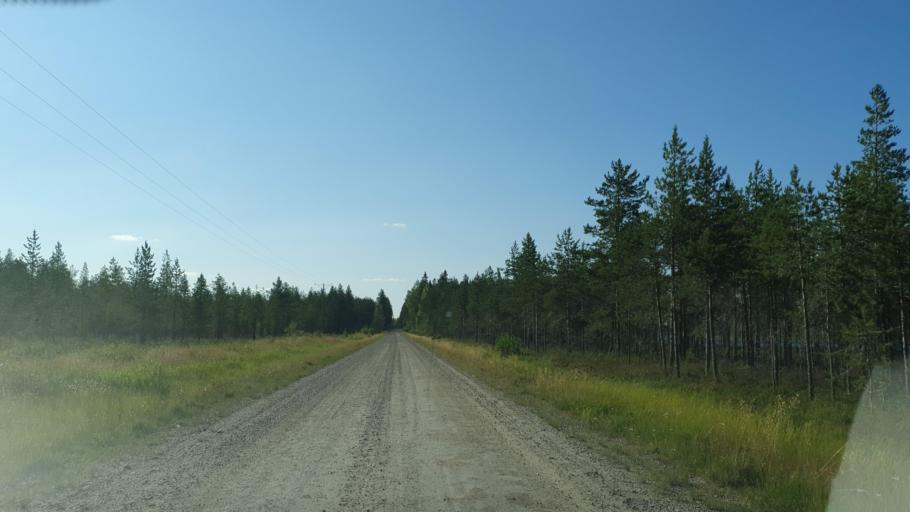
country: FI
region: Kainuu
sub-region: Kehys-Kainuu
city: Kuhmo
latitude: 64.0215
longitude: 29.7330
